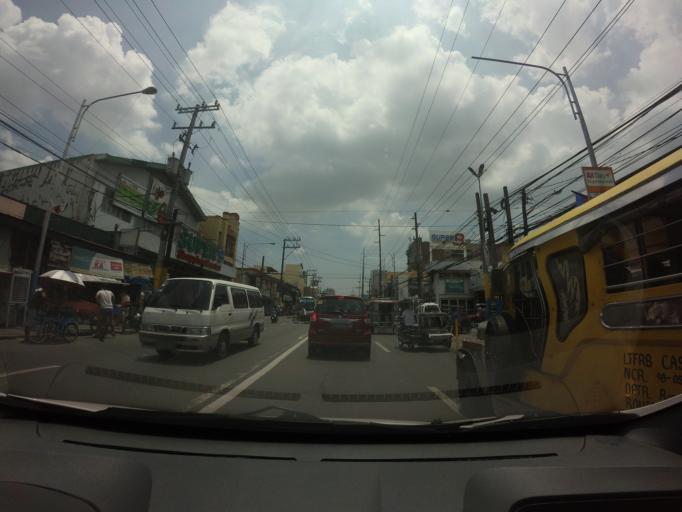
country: PH
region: Calabarzon
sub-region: Province of Laguna
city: San Pedro
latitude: 14.4092
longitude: 121.0464
